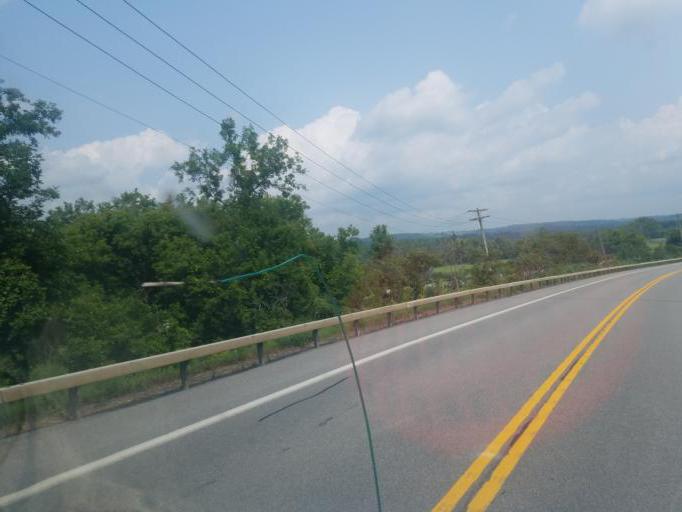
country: US
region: New York
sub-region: Herkimer County
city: Herkimer
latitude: 43.0135
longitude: -74.9408
